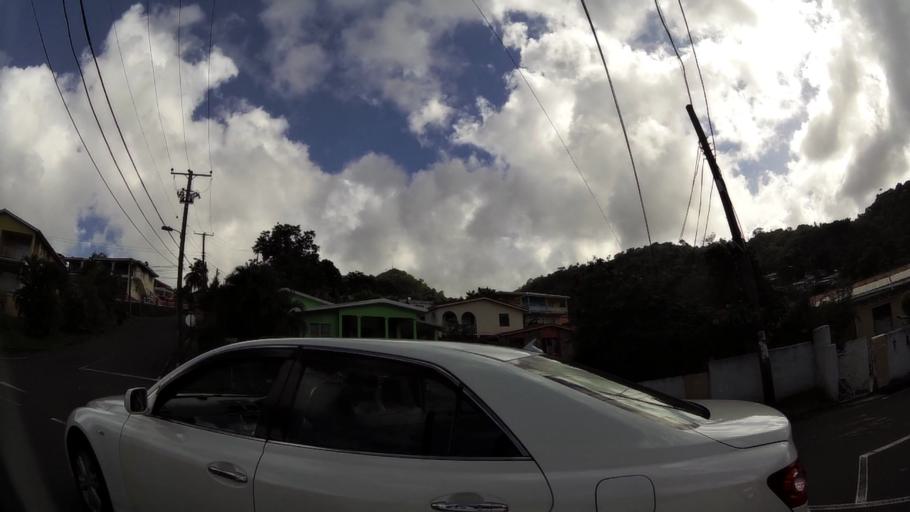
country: LC
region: Castries Quarter
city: Bisee
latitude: 14.0026
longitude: -60.9827
